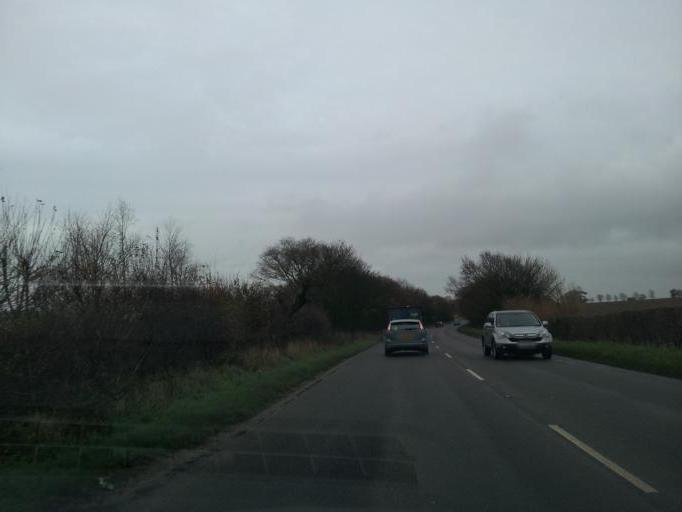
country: GB
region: England
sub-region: Norfolk
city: Martham
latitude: 52.6957
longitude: 1.6049
